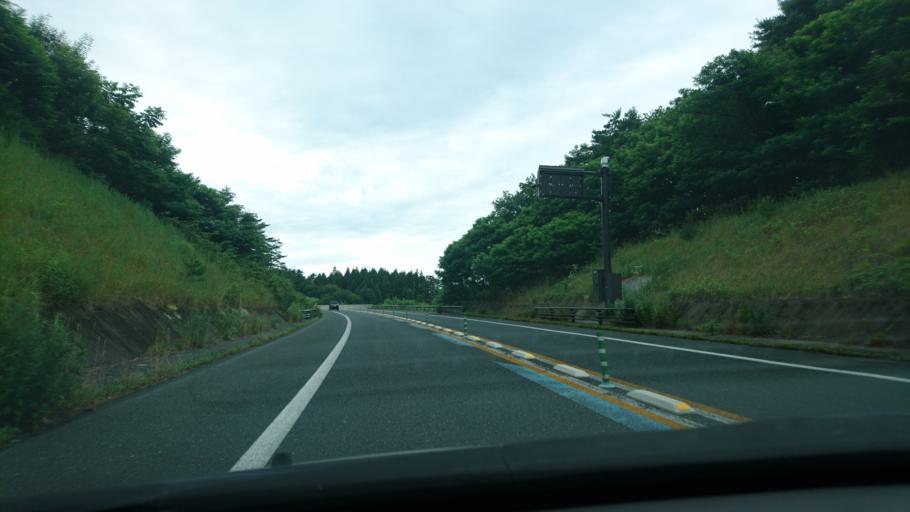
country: JP
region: Iwate
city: Miyako
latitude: 39.8753
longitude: 141.9361
